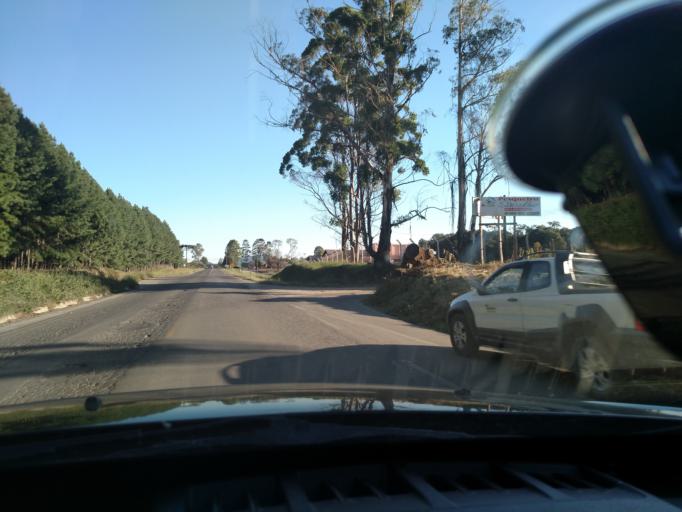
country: BR
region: Santa Catarina
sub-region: Lages
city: Lages
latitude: -27.7281
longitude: -50.2022
